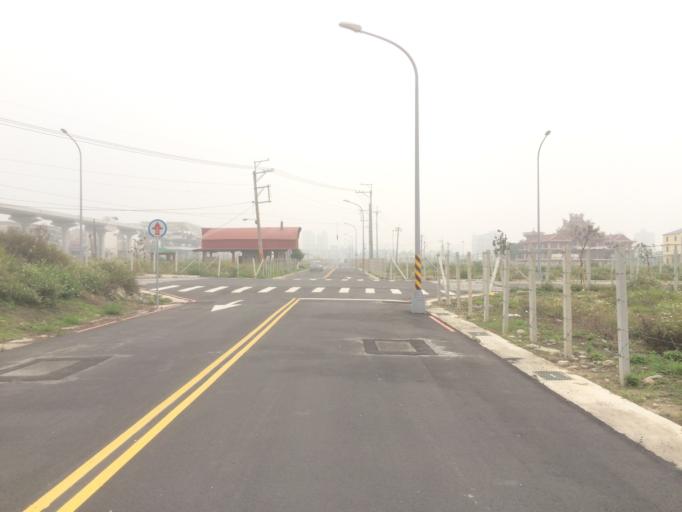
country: TW
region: Taiwan
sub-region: Taichung City
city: Taichung
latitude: 24.1813
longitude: 120.7036
